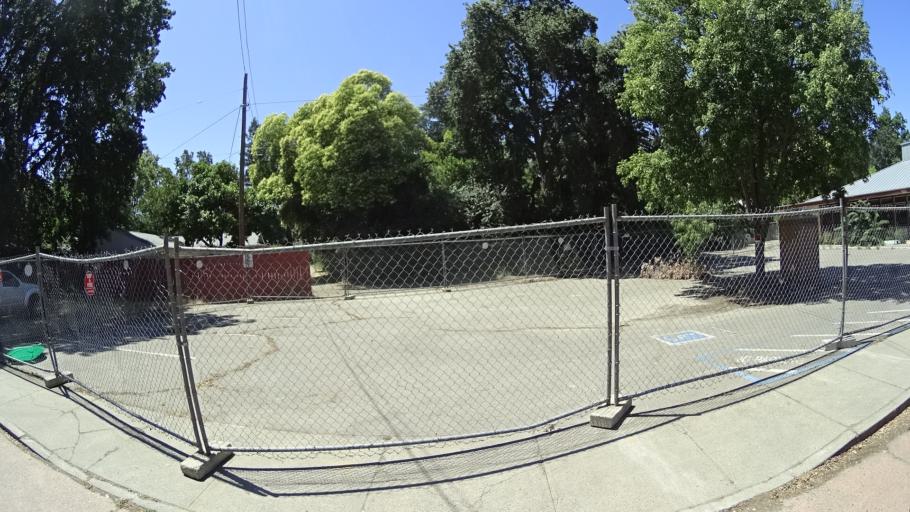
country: US
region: California
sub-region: Sacramento County
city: Sacramento
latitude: 38.5540
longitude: -121.4843
